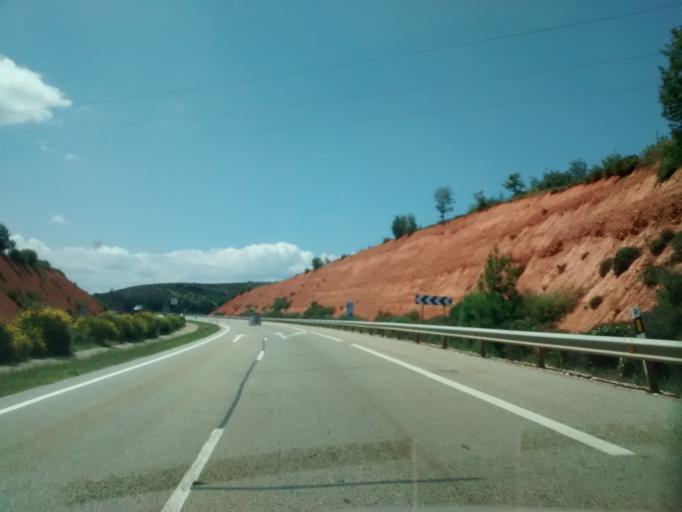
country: ES
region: Castille and Leon
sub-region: Provincia de Leon
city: Brazuelo
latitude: 42.4985
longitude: -6.1248
